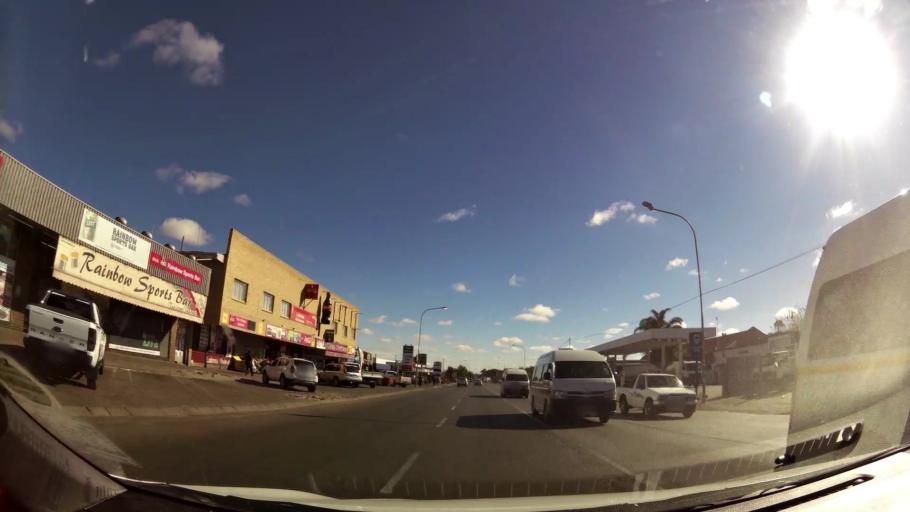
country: ZA
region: Limpopo
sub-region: Capricorn District Municipality
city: Polokwane
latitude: -23.8805
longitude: 29.4422
